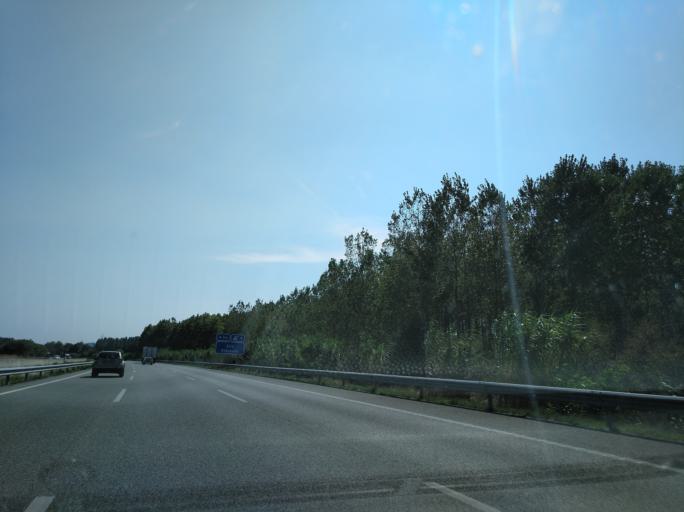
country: ES
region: Catalonia
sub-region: Provincia de Girona
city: Sils
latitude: 41.8248
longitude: 2.7464
